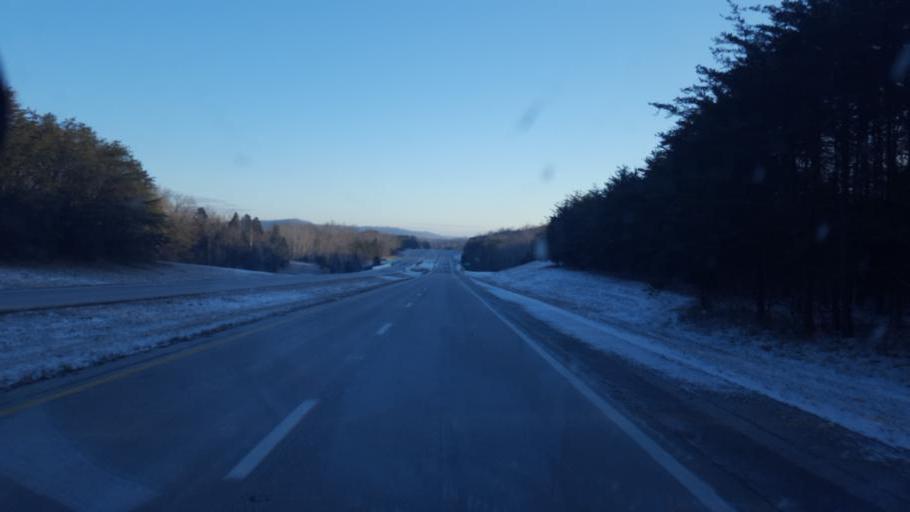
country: US
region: Ohio
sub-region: Adams County
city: Peebles
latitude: 38.9675
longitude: -83.3494
